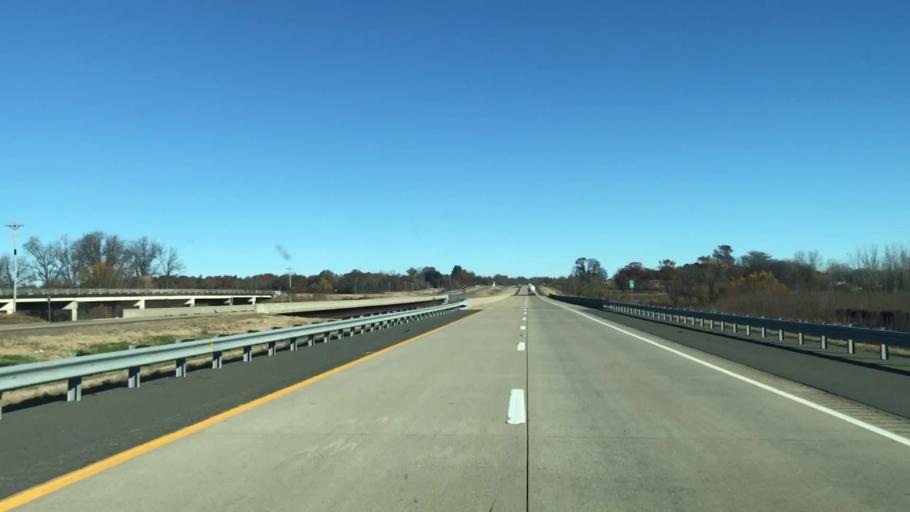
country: US
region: Texas
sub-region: Cass County
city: Queen City
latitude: 33.1476
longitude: -93.8914
